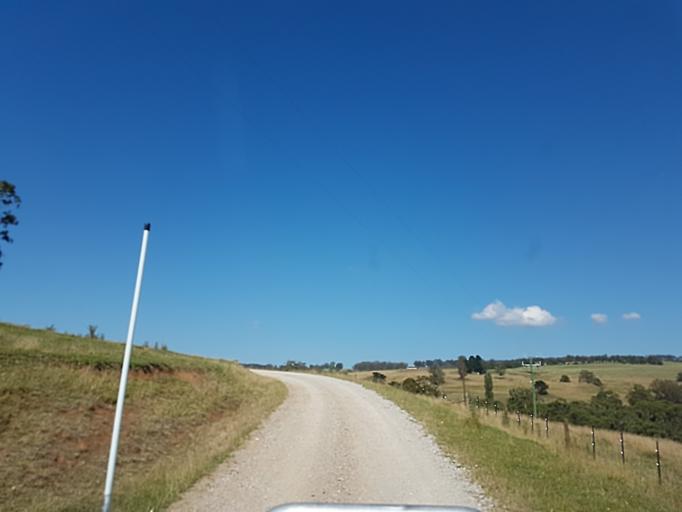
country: AU
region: Victoria
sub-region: East Gippsland
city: Lakes Entrance
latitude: -37.2316
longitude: 148.2631
